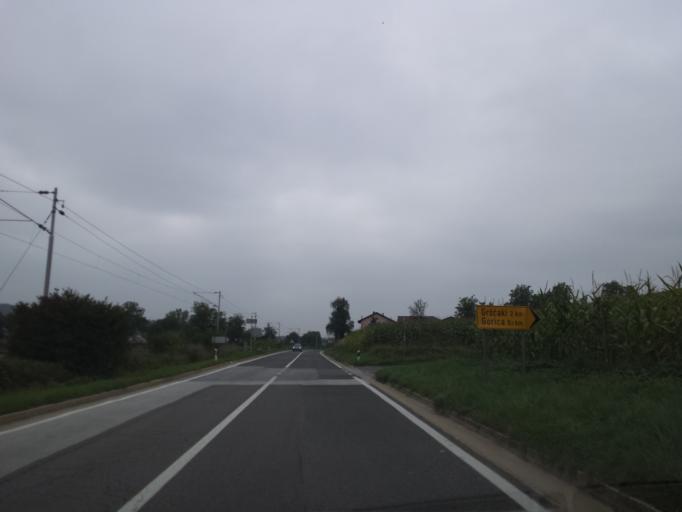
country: HR
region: Karlovacka
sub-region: Grad Karlovac
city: Karlovac
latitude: 45.4294
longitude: 15.4883
